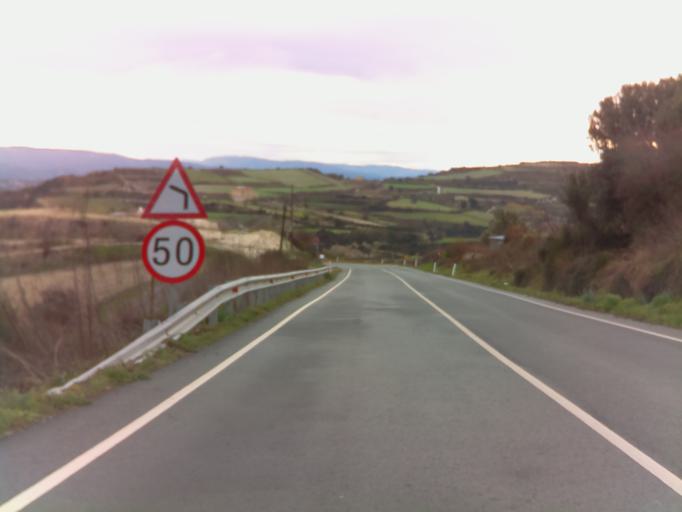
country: CY
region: Pafos
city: Tala
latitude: 34.8978
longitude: 32.4542
